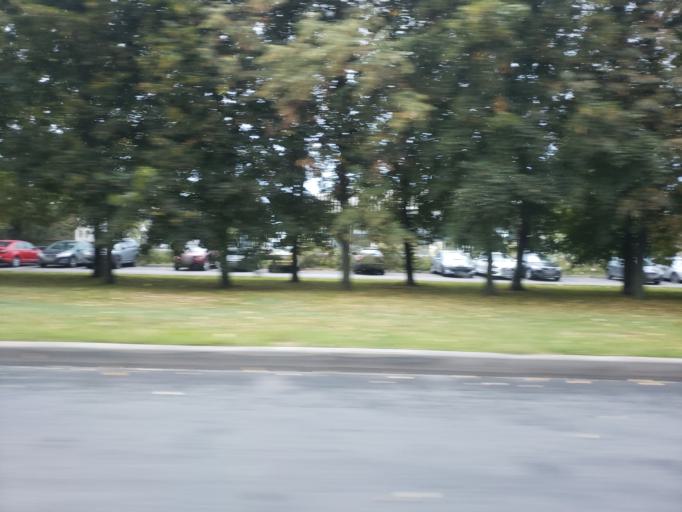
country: RU
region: St.-Petersburg
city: Vasyl'evsky Ostrov
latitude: 59.9276
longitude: 30.2379
